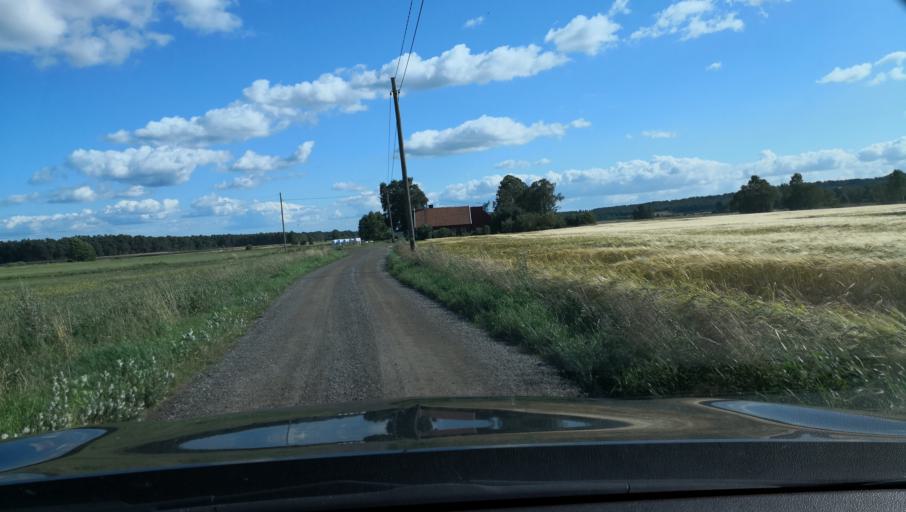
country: SE
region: Skane
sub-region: Kristianstads Kommun
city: Degeberga
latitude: 55.8093
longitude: 14.1892
